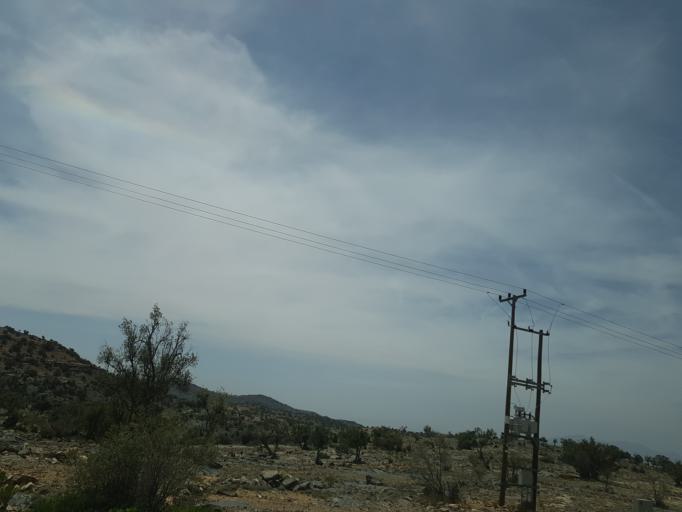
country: OM
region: Al Batinah
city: Bayt al `Awabi
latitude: 23.1288
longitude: 57.5981
